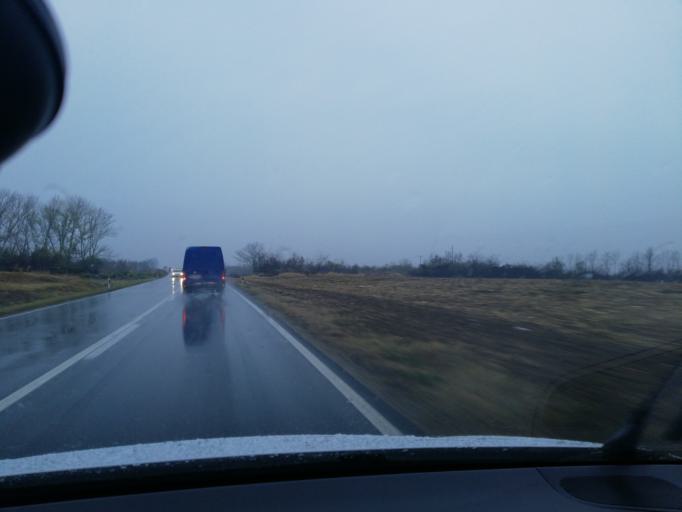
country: RS
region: Autonomna Pokrajina Vojvodina
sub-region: Sremski Okrug
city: Ruma
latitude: 45.0224
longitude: 19.8362
